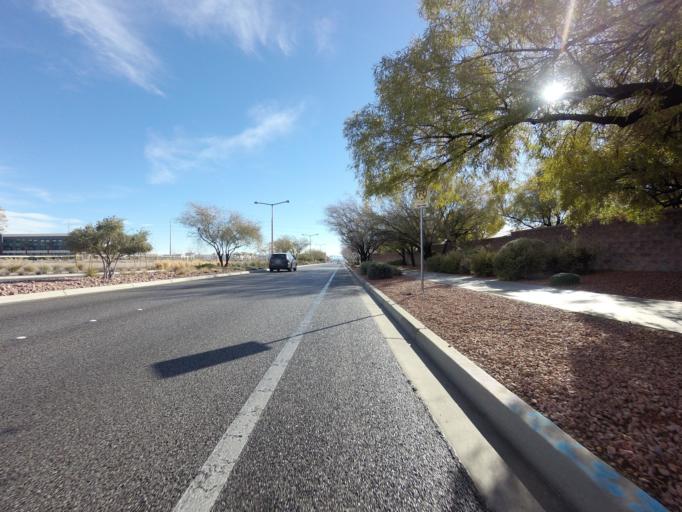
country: US
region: Nevada
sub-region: Clark County
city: Summerlin South
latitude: 36.1151
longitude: -115.3181
